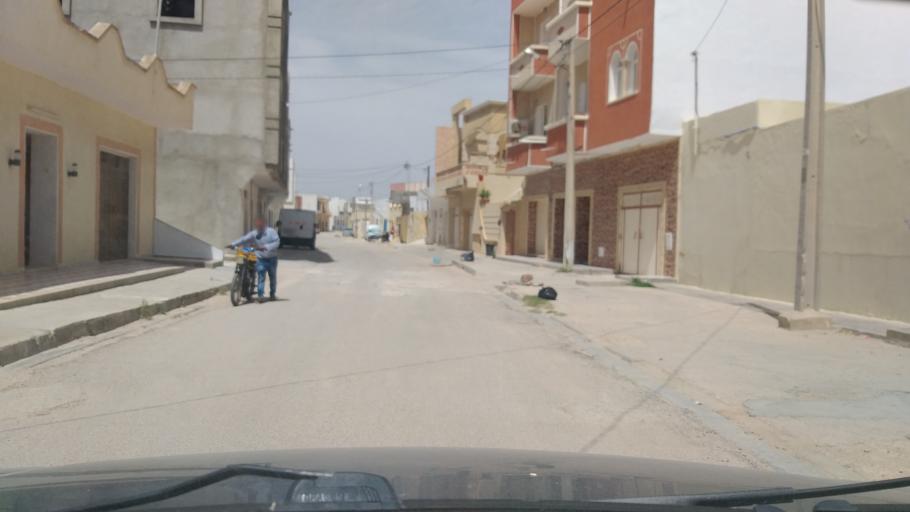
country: TN
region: Al Mahdiyah
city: El Jem
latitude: 35.2951
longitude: 10.6982
